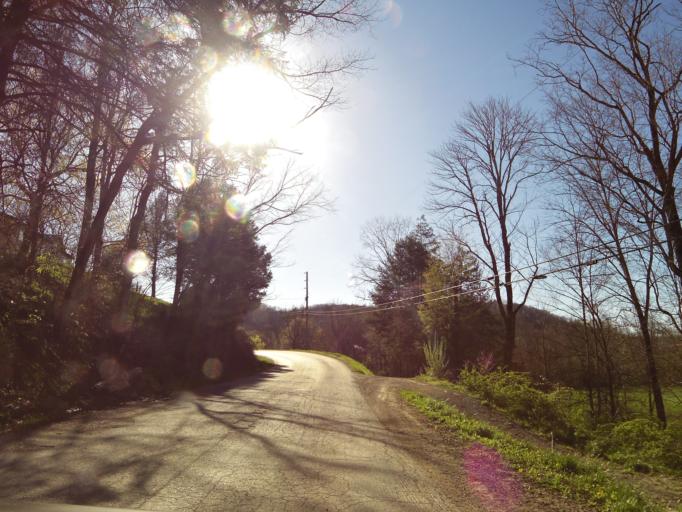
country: US
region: Tennessee
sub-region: Scott County
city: Huntsville
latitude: 36.3242
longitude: -84.3701
